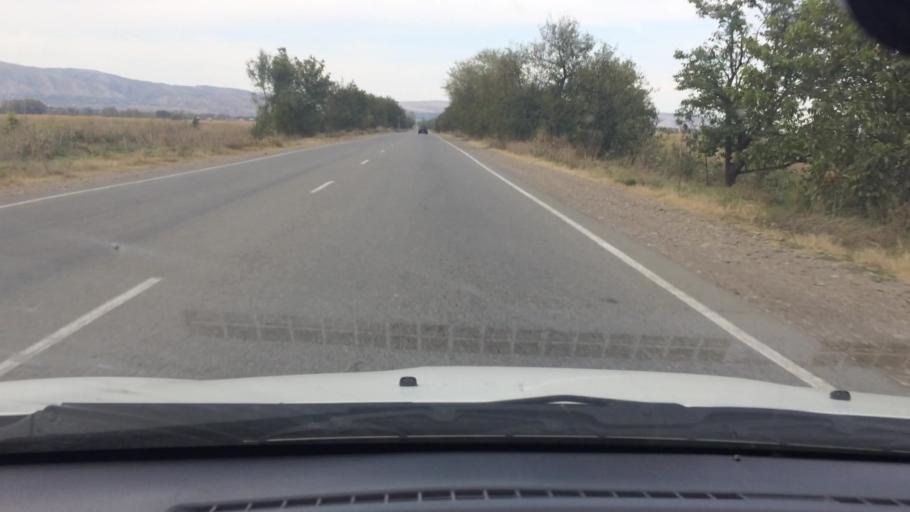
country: GE
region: Kvemo Kartli
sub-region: Marneuli
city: Marneuli
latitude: 41.5585
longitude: 44.7759
